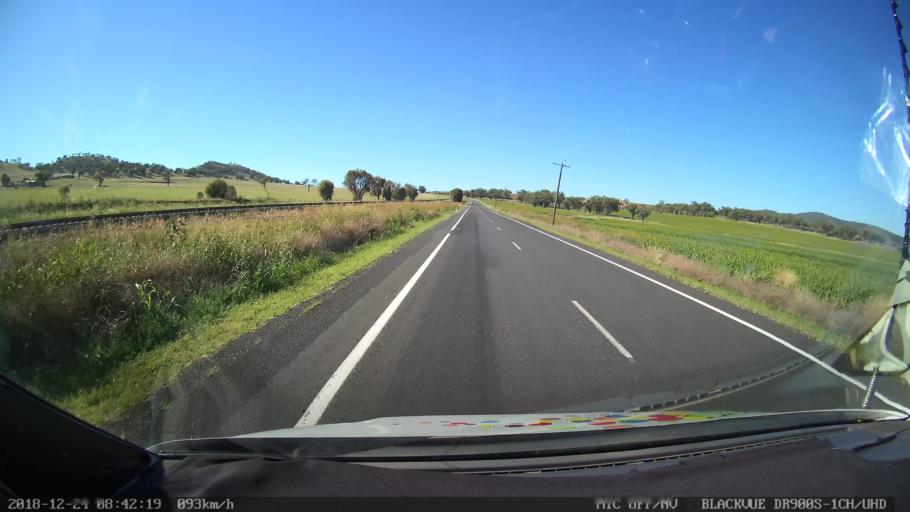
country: AU
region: New South Wales
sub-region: Liverpool Plains
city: Quirindi
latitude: -31.3731
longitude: 150.6432
